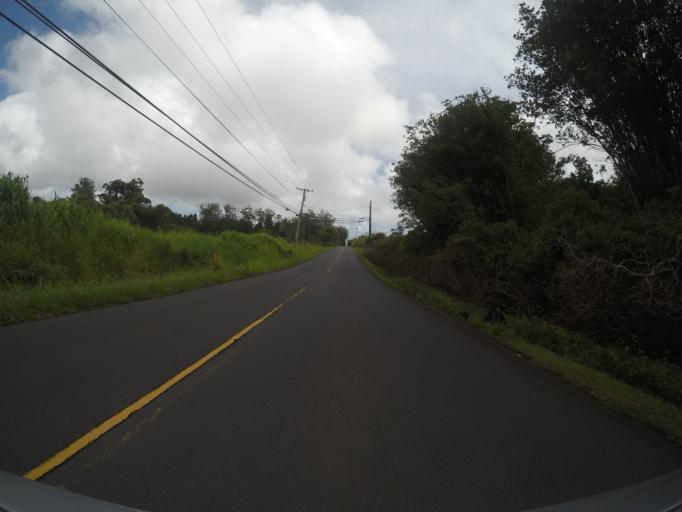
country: US
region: Hawaii
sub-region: Hawaii County
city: Fern Acres
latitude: 19.4849
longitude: -155.1506
